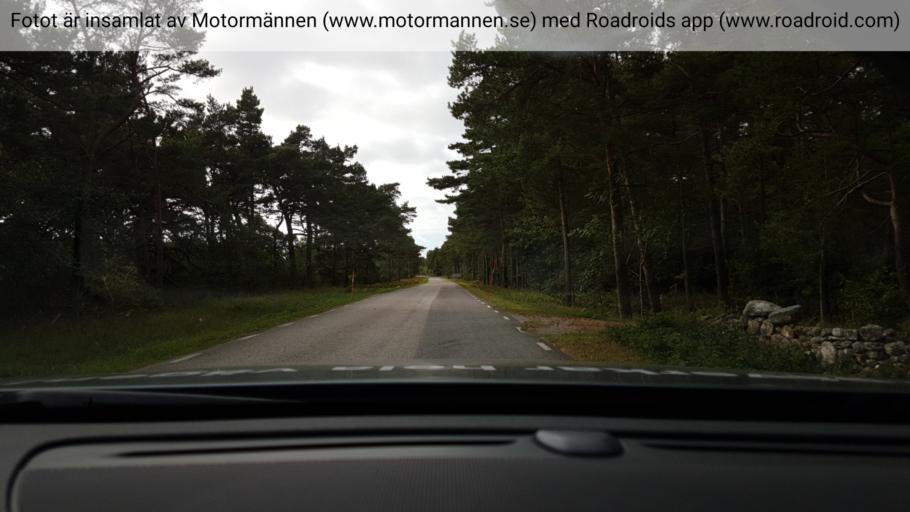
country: SE
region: Gotland
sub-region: Gotland
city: Hemse
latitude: 56.9578
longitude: 18.2171
